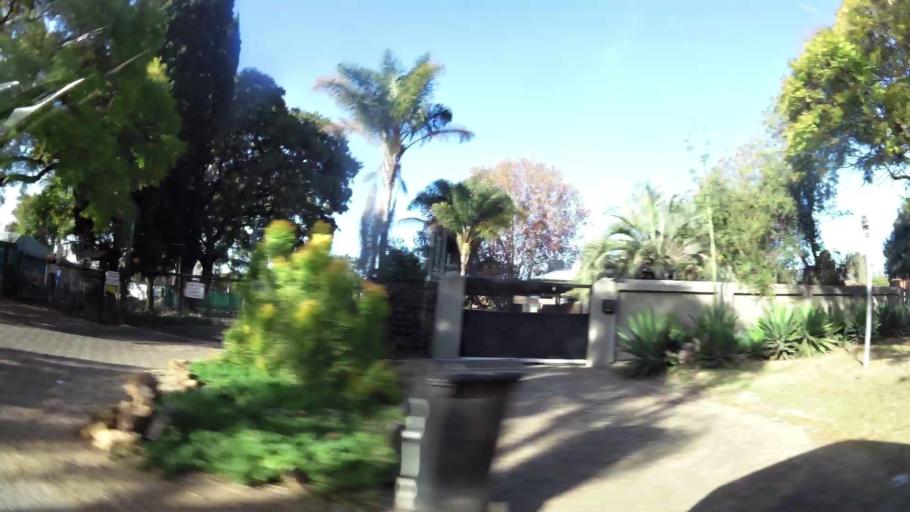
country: ZA
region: Gauteng
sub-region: City of Tshwane Metropolitan Municipality
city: Pretoria
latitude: -25.7250
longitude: 28.2130
